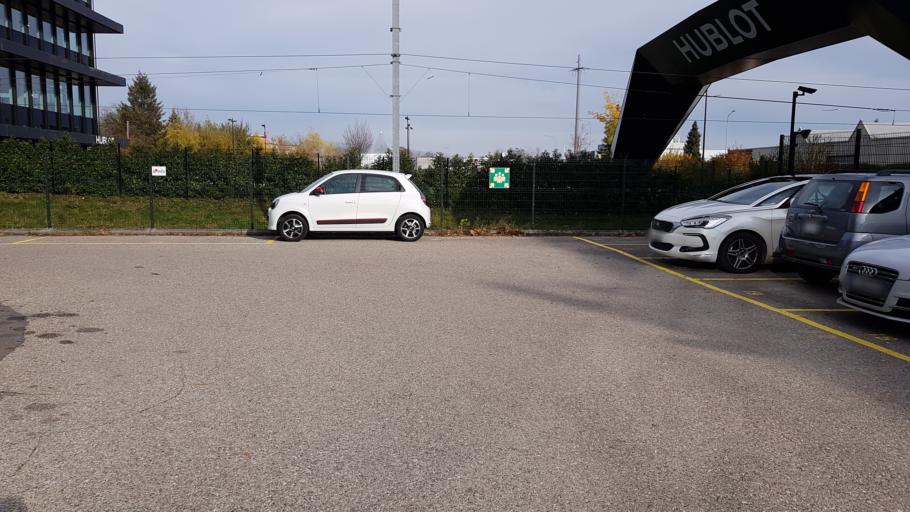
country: CH
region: Vaud
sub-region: Nyon District
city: Trelex
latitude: 46.3994
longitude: 6.2157
